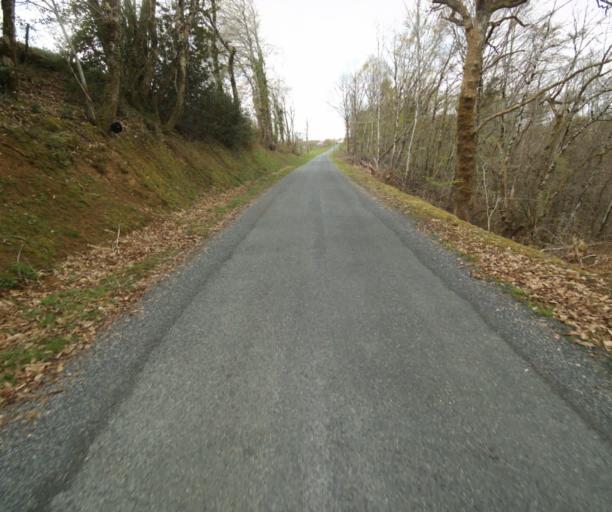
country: FR
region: Limousin
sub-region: Departement de la Correze
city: Sainte-Fortunade
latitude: 45.1927
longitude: 1.8621
